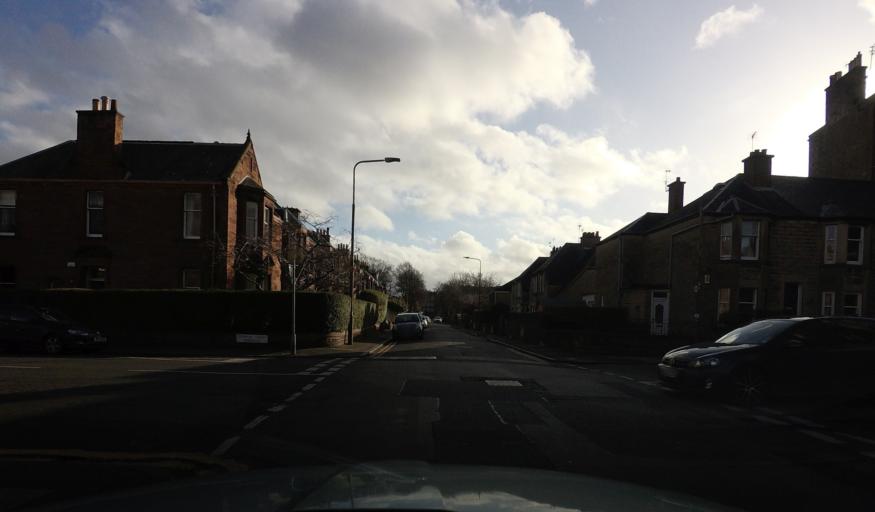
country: GB
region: Scotland
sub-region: Edinburgh
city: Edinburgh
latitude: 55.9738
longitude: -3.2091
